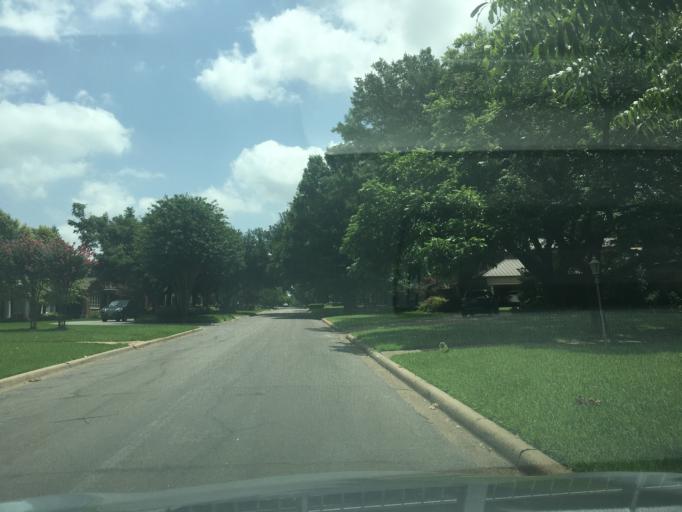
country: US
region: Texas
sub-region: Dallas County
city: University Park
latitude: 32.8769
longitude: -96.7906
